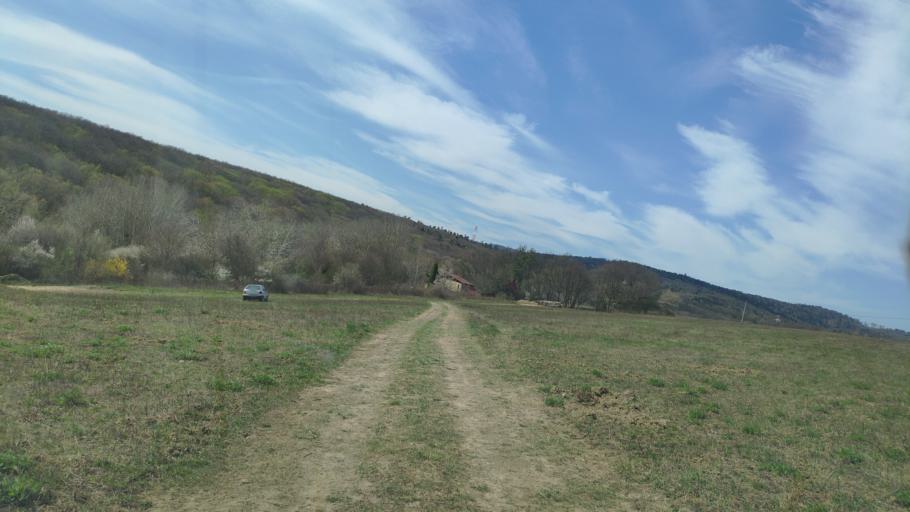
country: SK
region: Kosicky
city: Kosice
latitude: 48.7217
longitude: 21.1954
